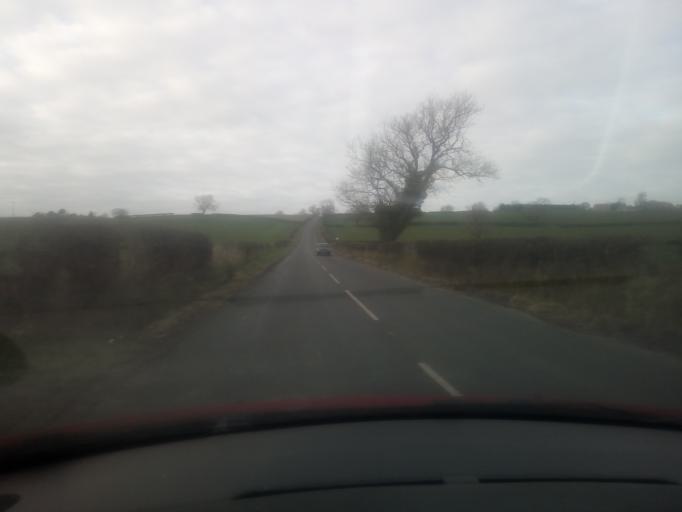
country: GB
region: England
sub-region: Darlington
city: Summerhouse
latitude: 54.5920
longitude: -1.6803
